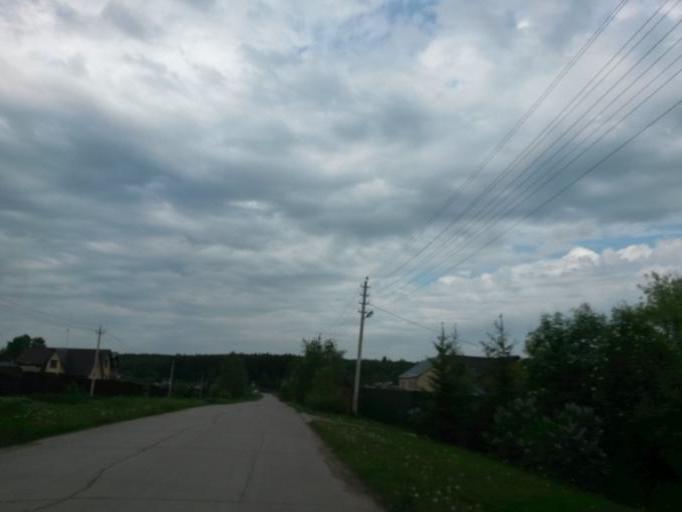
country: RU
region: Moskovskaya
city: Melikhovo
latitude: 55.1546
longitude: 37.6302
